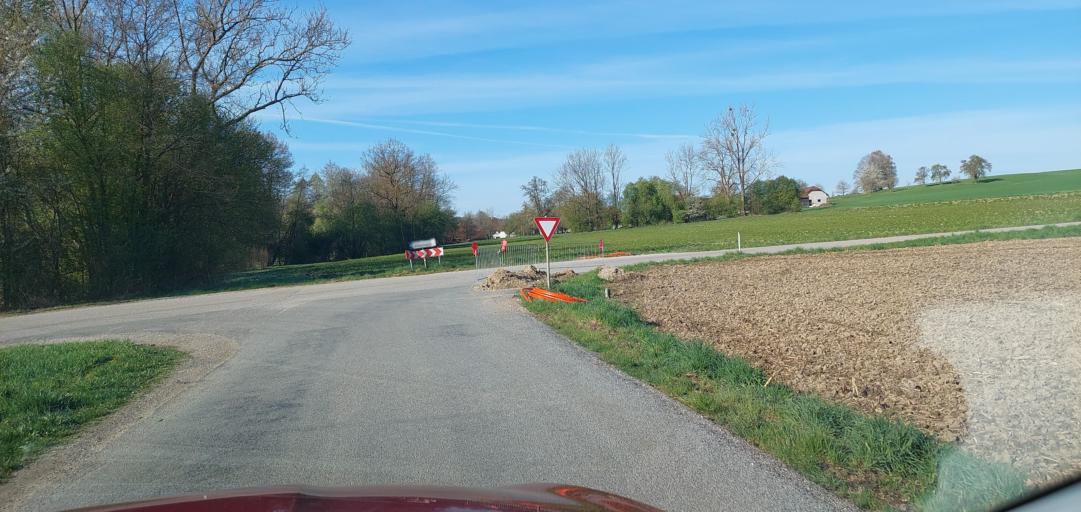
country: AT
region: Upper Austria
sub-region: Wels-Land
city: Offenhausen
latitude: 48.1663
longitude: 13.7988
